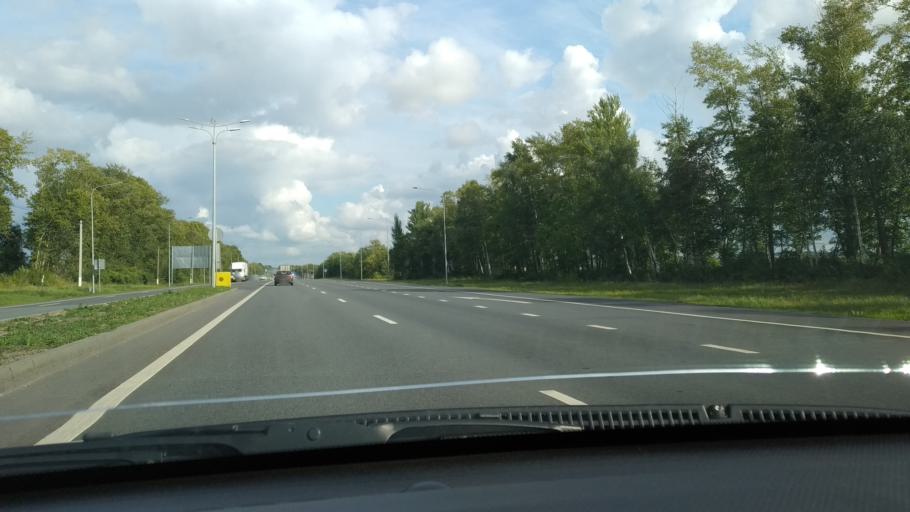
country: RU
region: Tatarstan
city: Stolbishchi
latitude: 55.6601
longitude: 49.3010
